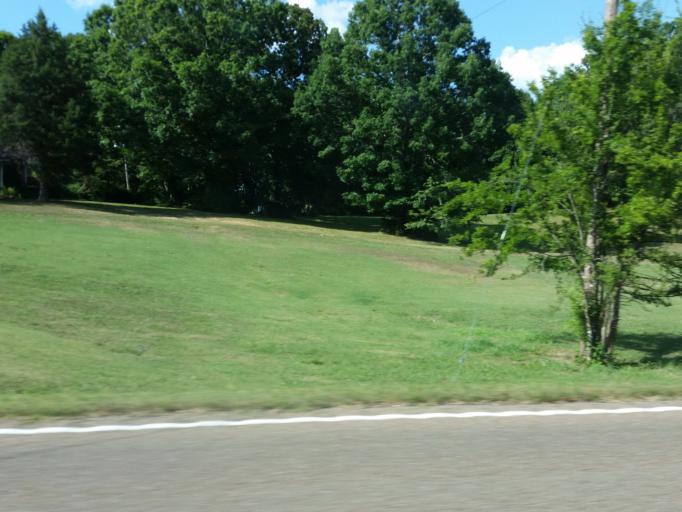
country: US
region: Tennessee
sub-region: Decatur County
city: Parsons
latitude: 35.6352
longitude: -88.0655
